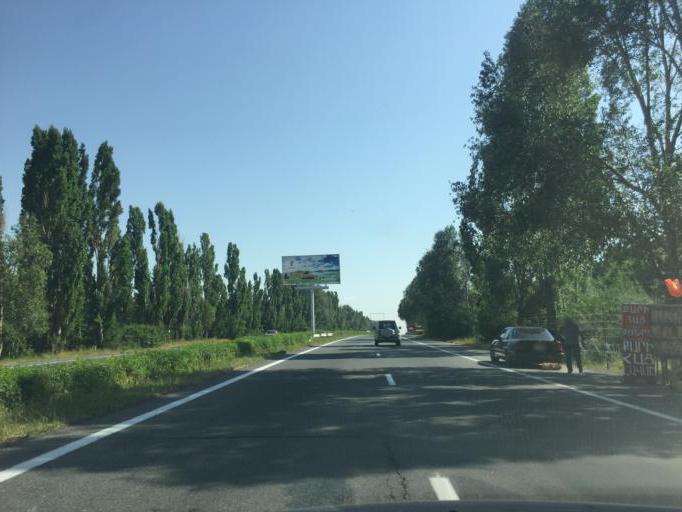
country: AM
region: Kotayk'i Marz
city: Fantan
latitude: 40.3859
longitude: 44.6576
